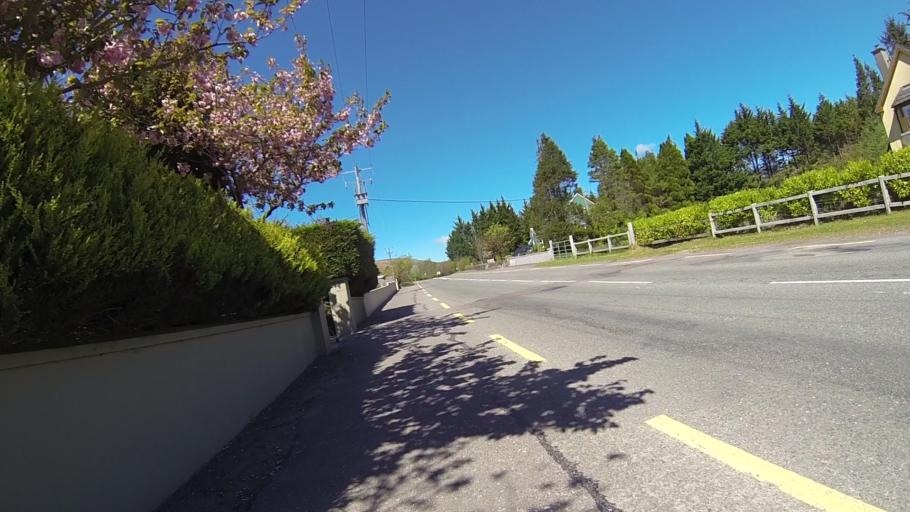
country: IE
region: Munster
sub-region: Ciarrai
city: Kenmare
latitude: 51.8859
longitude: -9.5953
